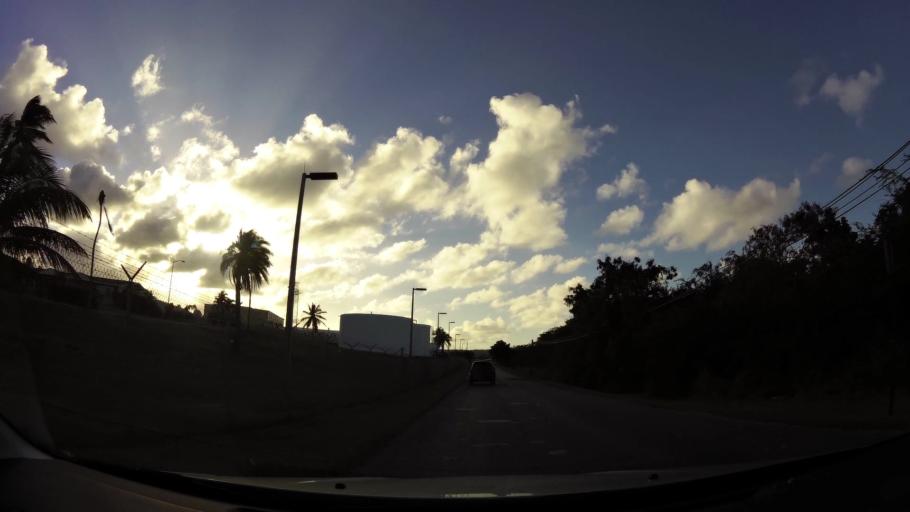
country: AG
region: Saint George
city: Piggotts
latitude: 17.1513
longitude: -61.7921
